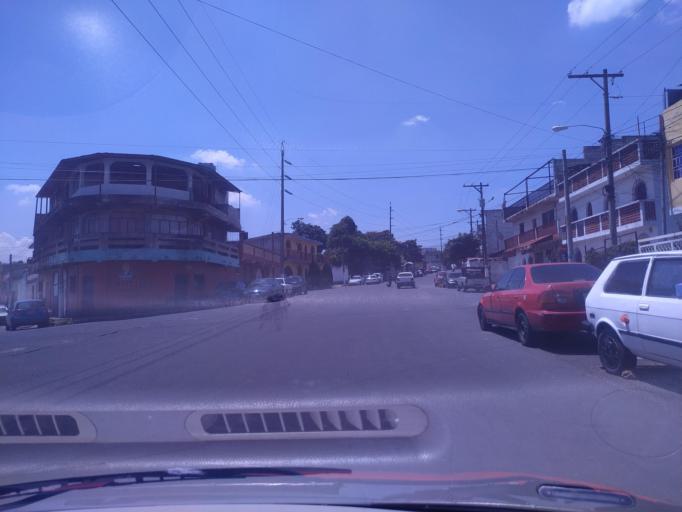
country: GT
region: Guatemala
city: Mixco
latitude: 14.6815
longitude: -90.5696
